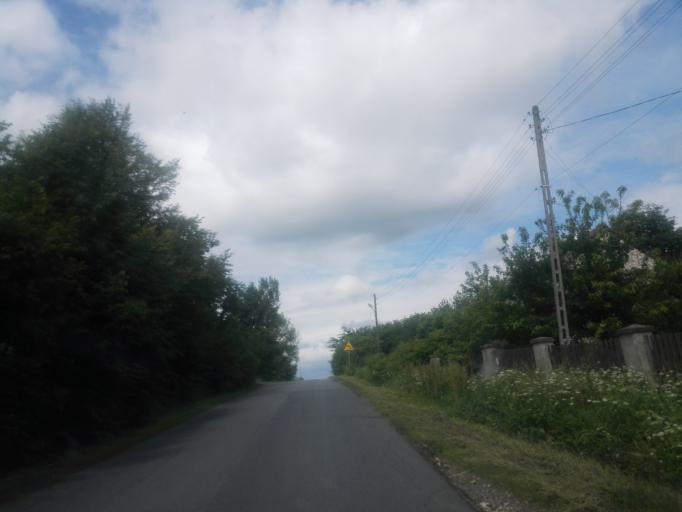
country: PL
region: Silesian Voivodeship
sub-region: Powiat myszkowski
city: Choron
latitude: 50.7073
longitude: 19.2892
